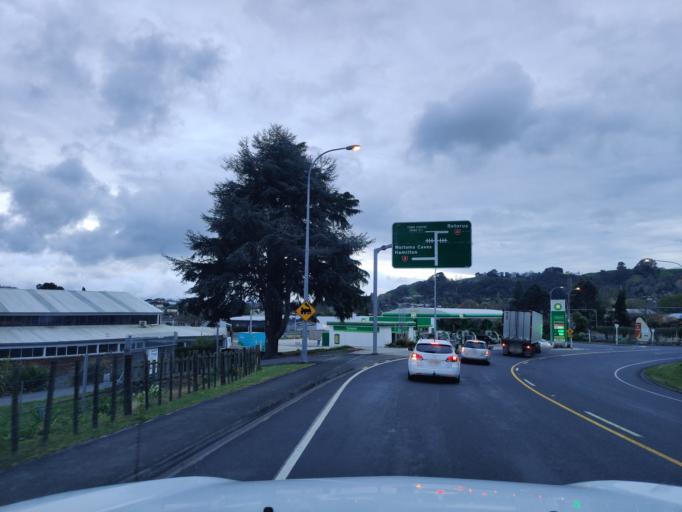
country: NZ
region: Waikato
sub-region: Otorohanga District
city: Otorohanga
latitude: -38.3390
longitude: 175.1670
